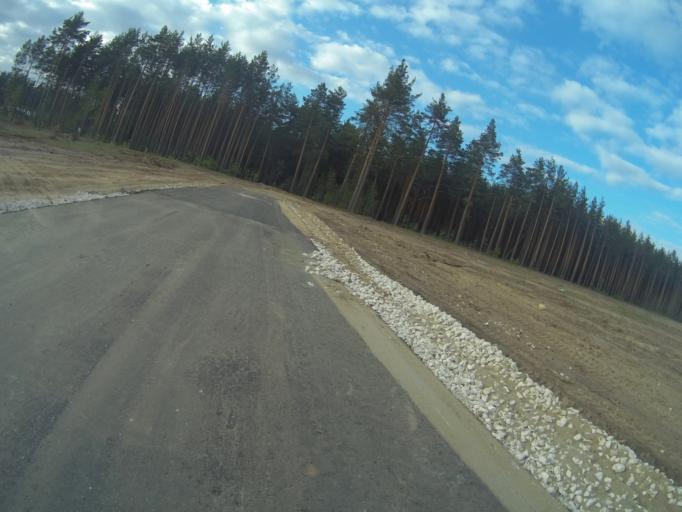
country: RU
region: Vladimir
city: Golovino
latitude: 56.0311
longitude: 40.4177
